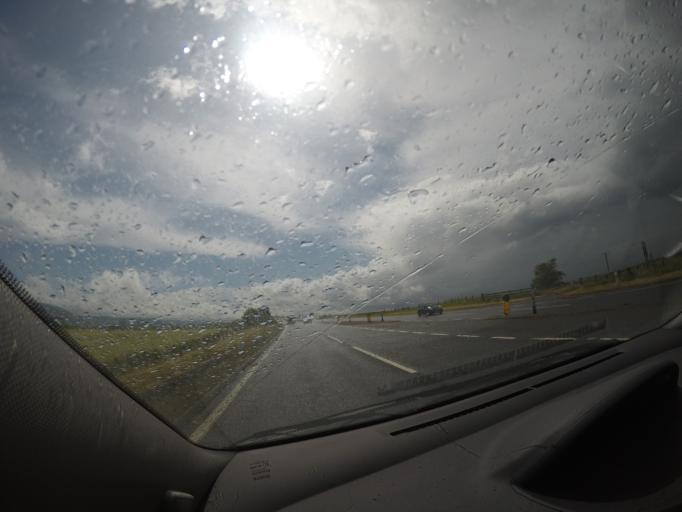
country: GB
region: Scotland
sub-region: Perth and Kinross
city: Auchterarder
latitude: 56.3315
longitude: -3.6330
